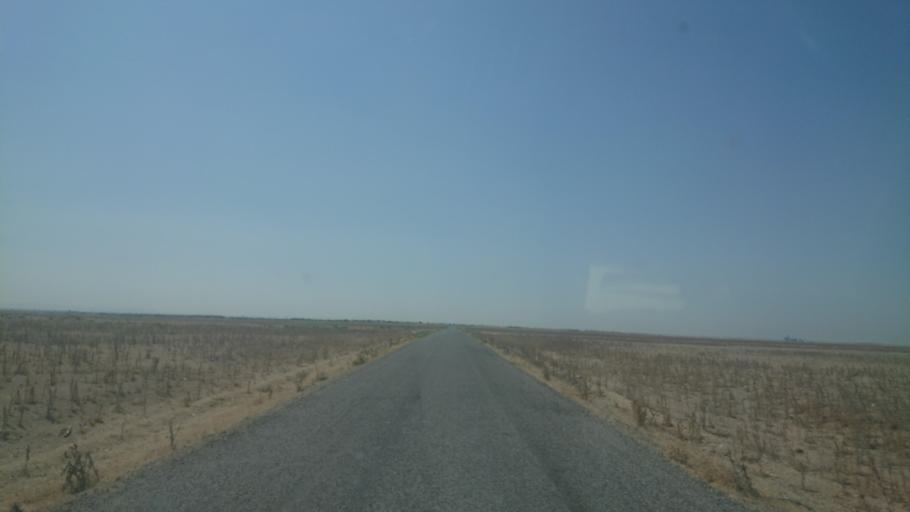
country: TR
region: Aksaray
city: Yesilova
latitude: 38.3136
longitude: 33.7390
